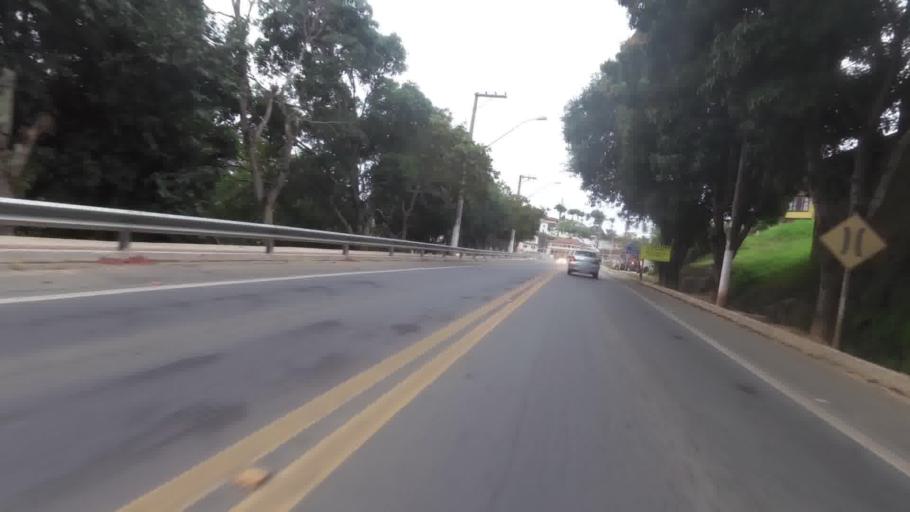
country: BR
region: Espirito Santo
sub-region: Piuma
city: Piuma
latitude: -20.8067
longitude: -40.6568
